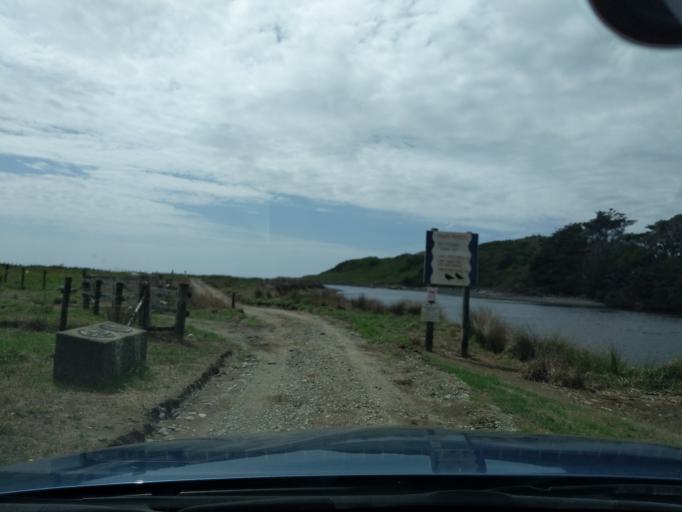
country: NZ
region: Tasman
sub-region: Tasman District
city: Takaka
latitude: -40.6433
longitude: 172.4320
